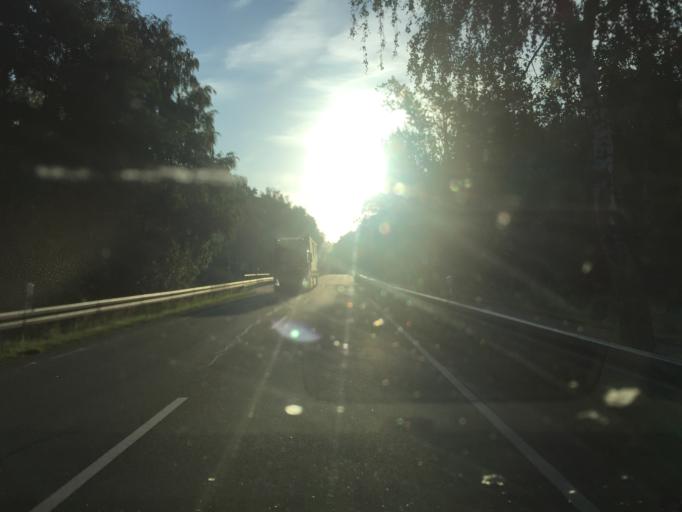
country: DE
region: Lower Saxony
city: Rethem
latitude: 52.7516
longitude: 9.3406
